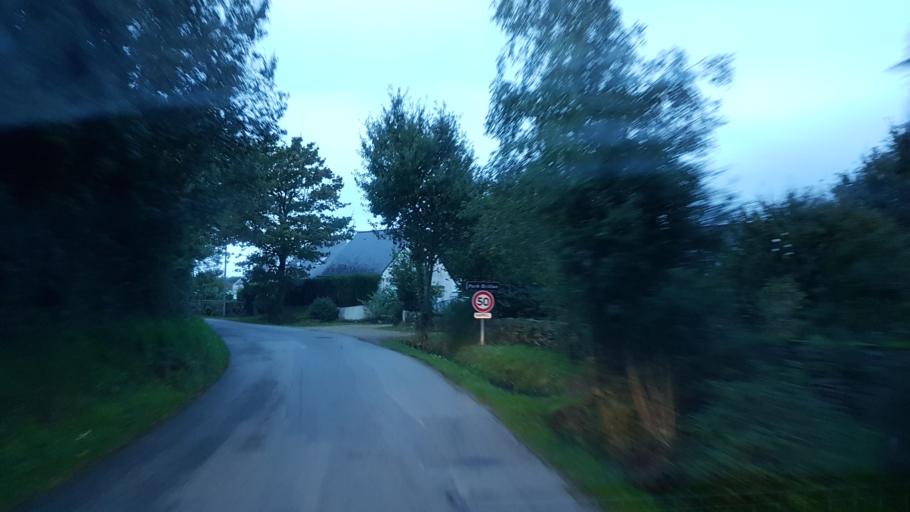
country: FR
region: Brittany
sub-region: Departement du Morbihan
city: Sarzeau
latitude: 47.5414
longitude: -2.8089
